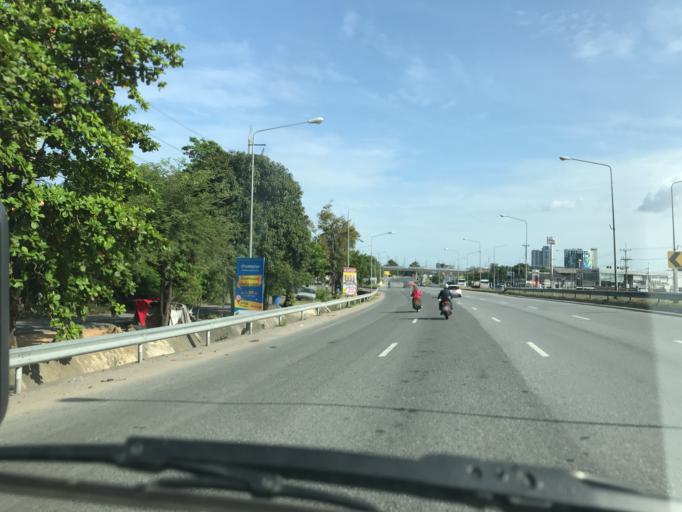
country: TH
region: Chon Buri
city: Bang Lamung
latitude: 13.0679
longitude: 100.9245
